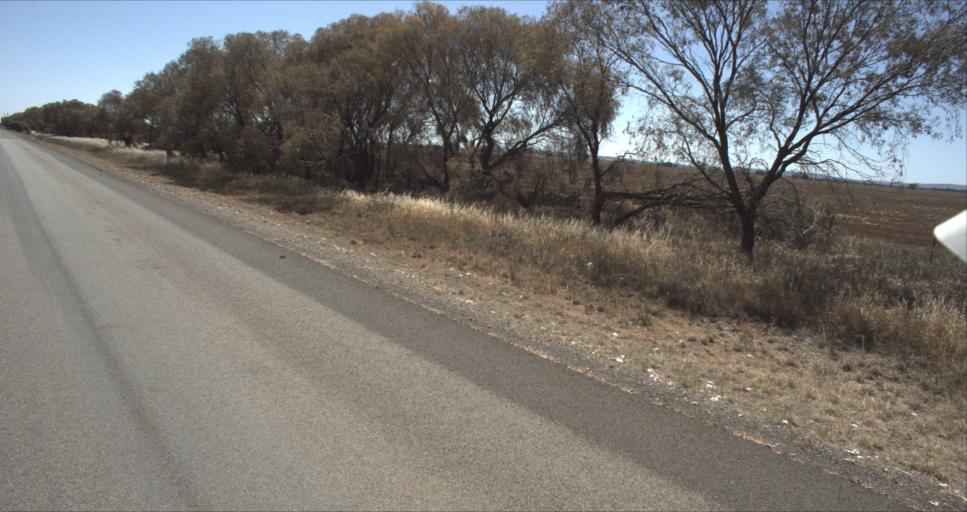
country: AU
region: New South Wales
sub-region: Leeton
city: Leeton
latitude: -34.4790
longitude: 146.2909
